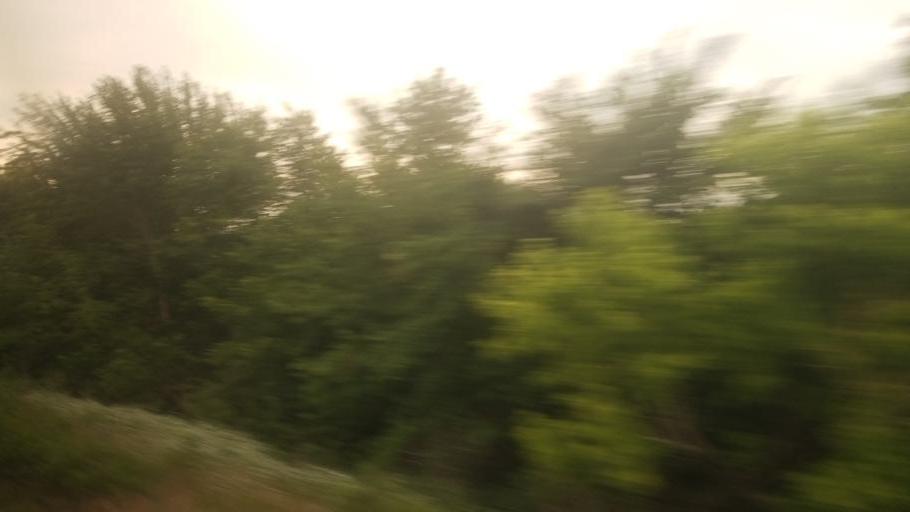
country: US
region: Kansas
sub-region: Chase County
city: Cottonwood Falls
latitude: 38.3855
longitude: -96.4859
